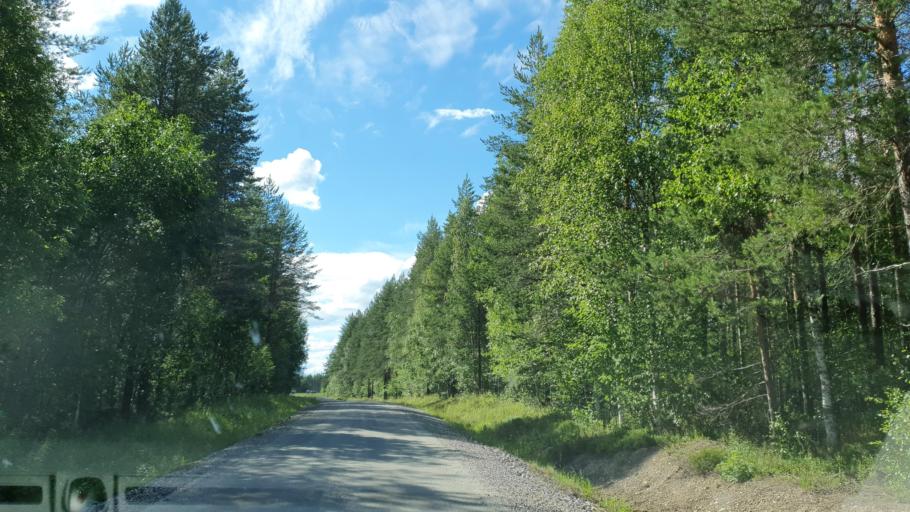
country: FI
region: Kainuu
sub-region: Kehys-Kainuu
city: Kuhmo
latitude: 64.1466
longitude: 29.7647
